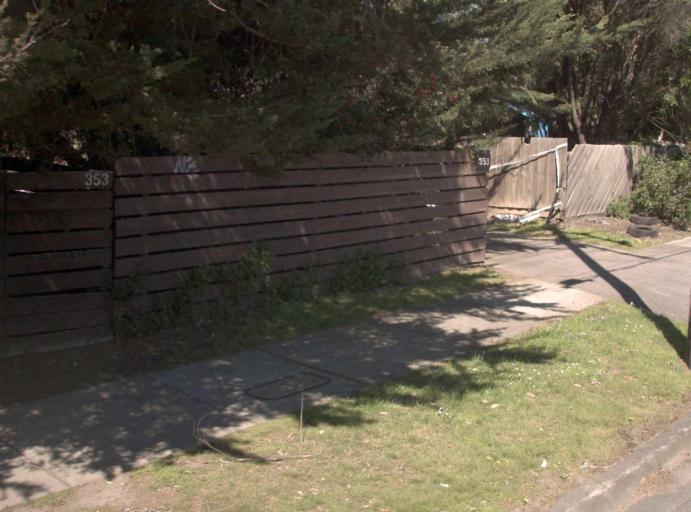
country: AU
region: Victoria
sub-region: Knox
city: Bayswater
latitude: -37.8332
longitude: 145.2700
